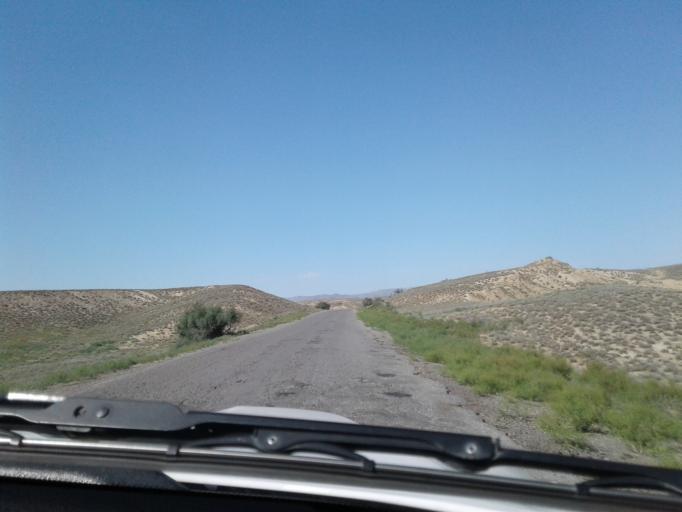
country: TM
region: Balkan
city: Magtymguly
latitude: 38.6667
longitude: 56.2869
